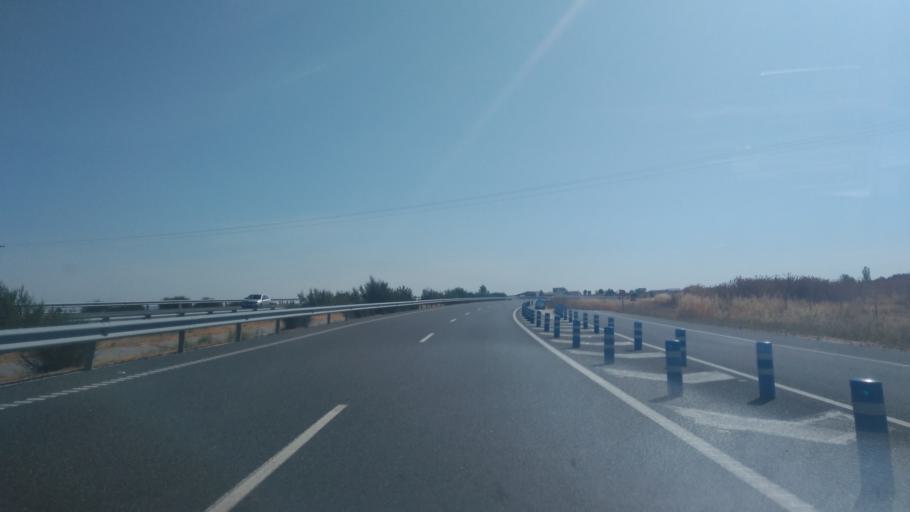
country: ES
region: Castille and Leon
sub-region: Provincia de Salamanca
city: Santa Marta de Tormes
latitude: 40.9447
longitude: -5.6044
